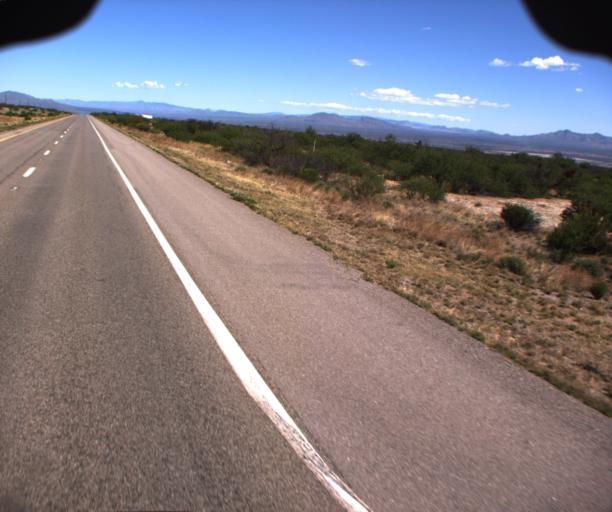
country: US
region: Arizona
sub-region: Cochise County
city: Whetstone
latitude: 31.9012
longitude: -110.3410
